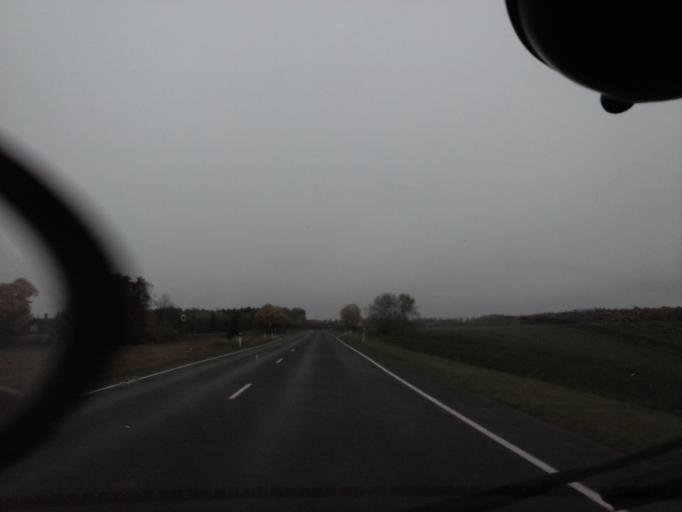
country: EE
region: Viljandimaa
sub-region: Vohma linn
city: Vohma
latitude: 58.7040
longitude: 25.6219
